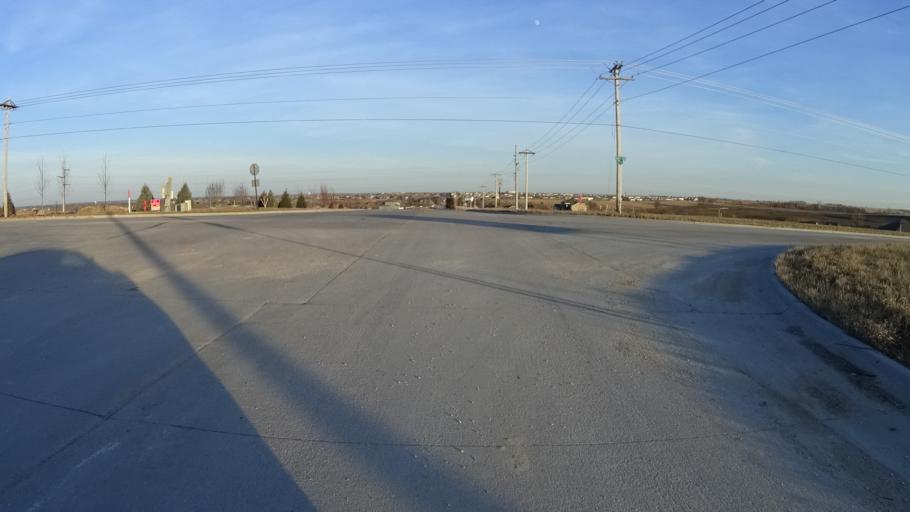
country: US
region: Nebraska
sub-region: Sarpy County
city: Papillion
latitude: 41.1326
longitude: -96.0912
